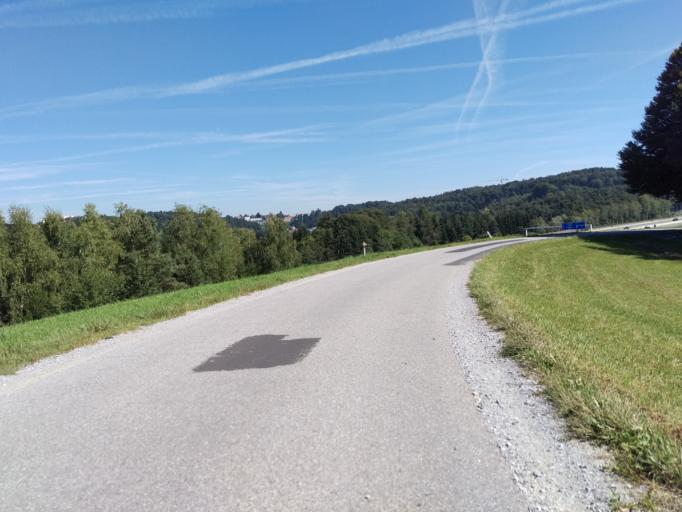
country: AT
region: Styria
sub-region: Politischer Bezirk Graz-Umgebung
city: Nestelbach bei Graz
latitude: 47.0624
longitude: 15.5750
